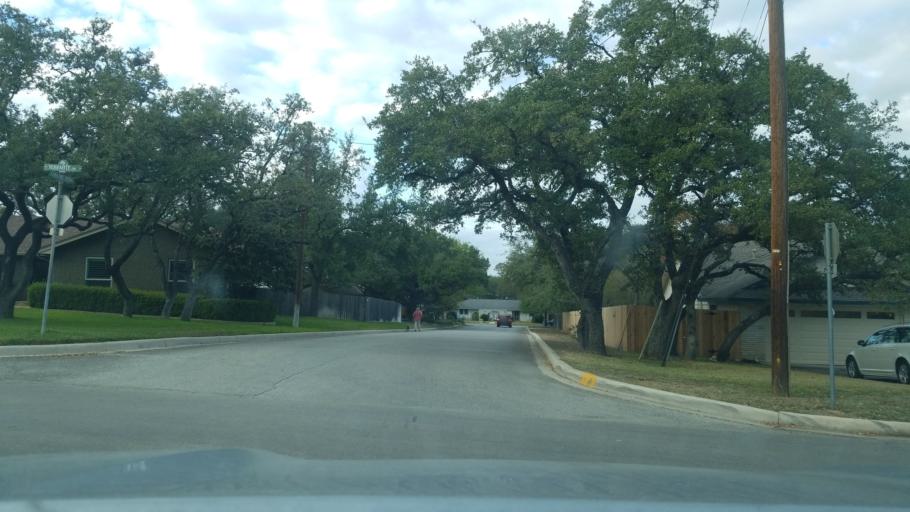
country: US
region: Texas
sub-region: Bexar County
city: Hollywood Park
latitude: 29.6037
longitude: -98.4844
